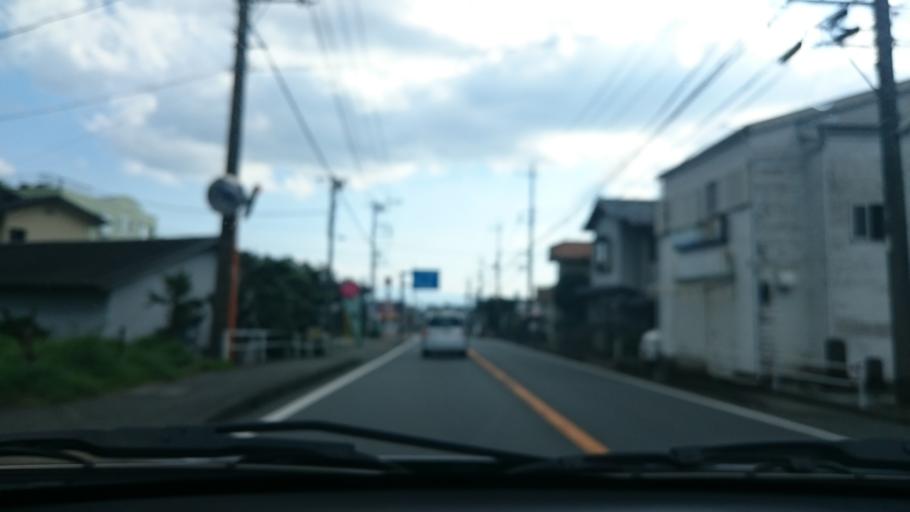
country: JP
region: Shizuoka
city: Gotemba
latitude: 35.2189
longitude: 138.9211
